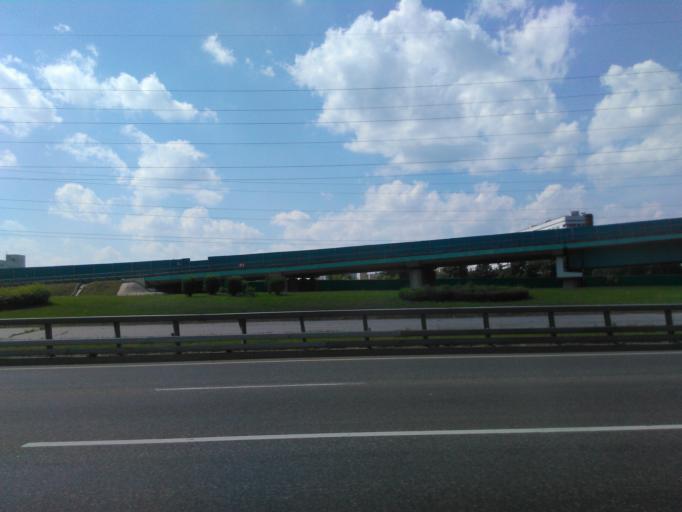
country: RU
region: Moskovskaya
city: Kuskovo
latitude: 55.7296
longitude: 37.8400
